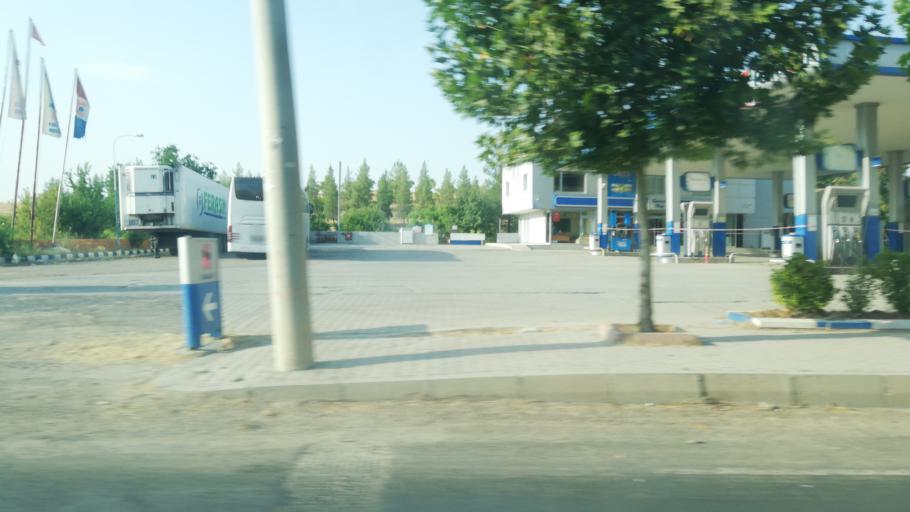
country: TR
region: Mardin
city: Midyat
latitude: 37.4337
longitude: 41.3313
